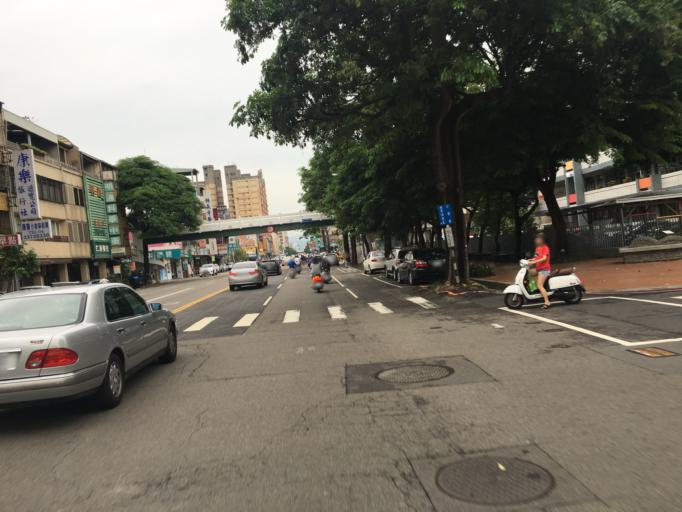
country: TW
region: Taiwan
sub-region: Taichung City
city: Taichung
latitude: 24.1398
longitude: 120.6682
